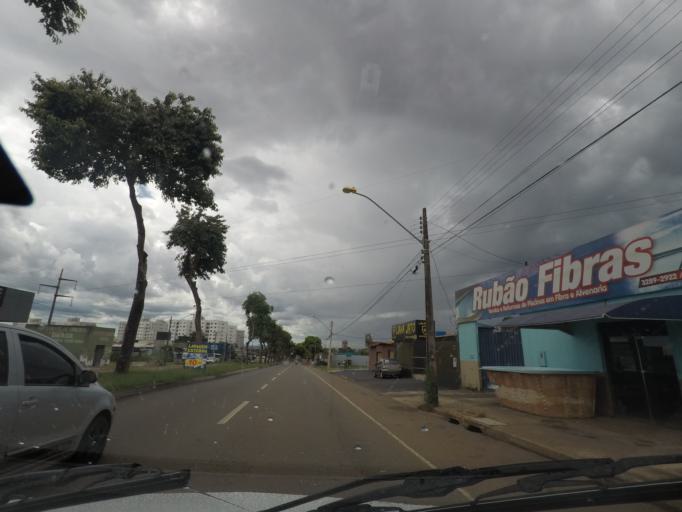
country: BR
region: Goias
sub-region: Goiania
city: Goiania
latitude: -16.7357
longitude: -49.3267
